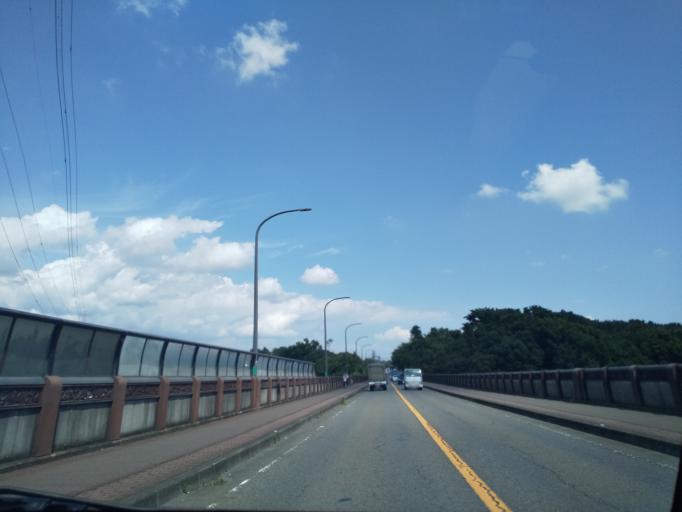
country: JP
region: Kanagawa
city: Zama
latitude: 35.4912
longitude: 139.4117
